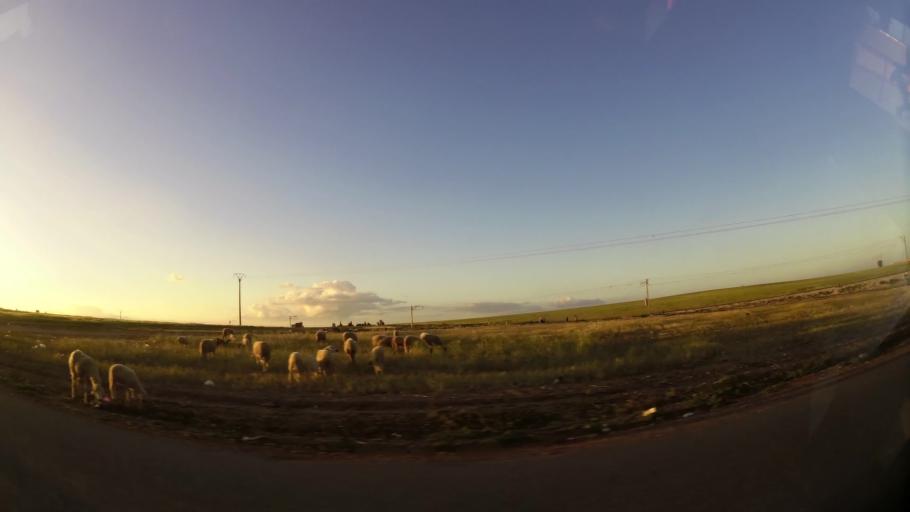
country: MA
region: Marrakech-Tensift-Al Haouz
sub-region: Kelaa-Des-Sraghna
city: Sidi Abdallah
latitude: 32.2405
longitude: -7.9322
